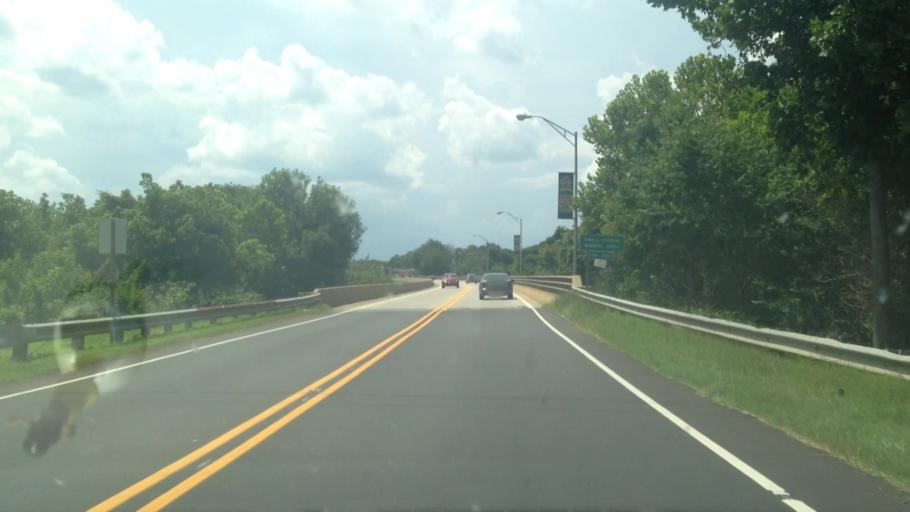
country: US
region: North Carolina
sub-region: Rockingham County
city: Madison
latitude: 36.3849
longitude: -79.9535
